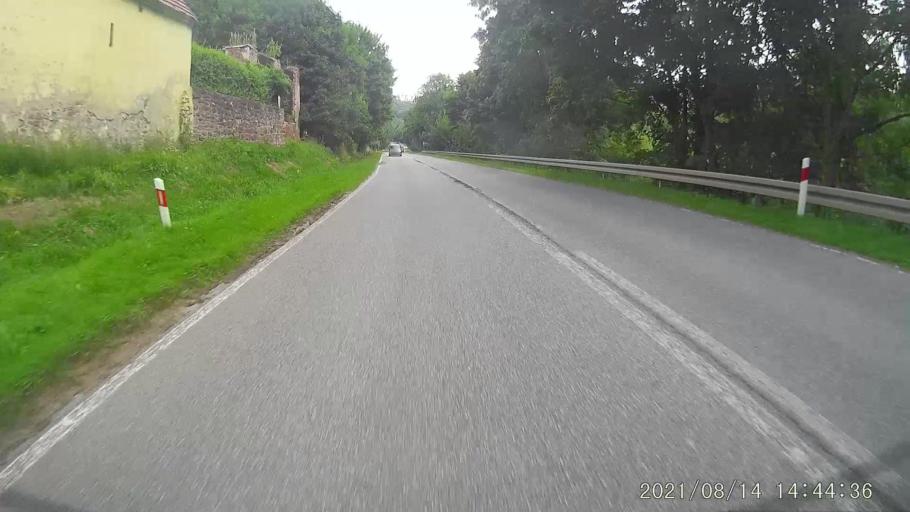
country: PL
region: Lower Silesian Voivodeship
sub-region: Powiat klodzki
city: Ludwikowice Klodzkie
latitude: 50.6302
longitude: 16.4397
